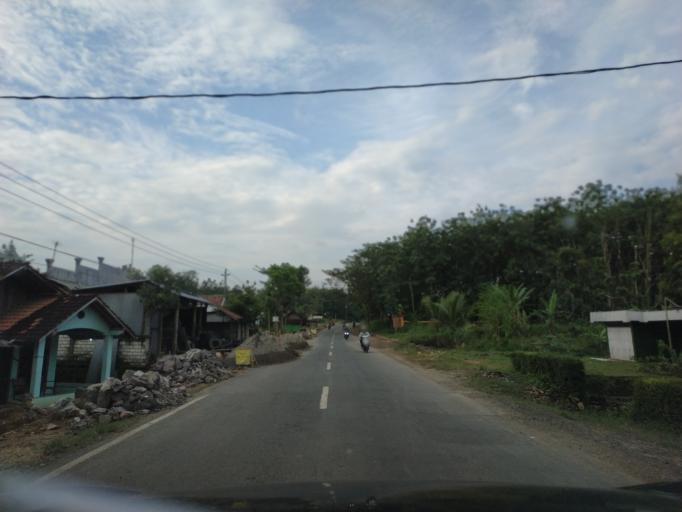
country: ID
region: Central Java
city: Medang
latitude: -6.9057
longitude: 111.4416
